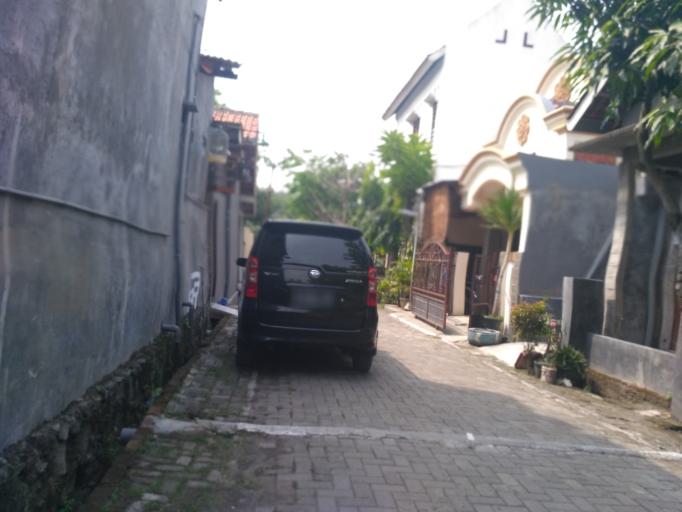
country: ID
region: Central Java
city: Mranggen
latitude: -7.0597
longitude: 110.4671
